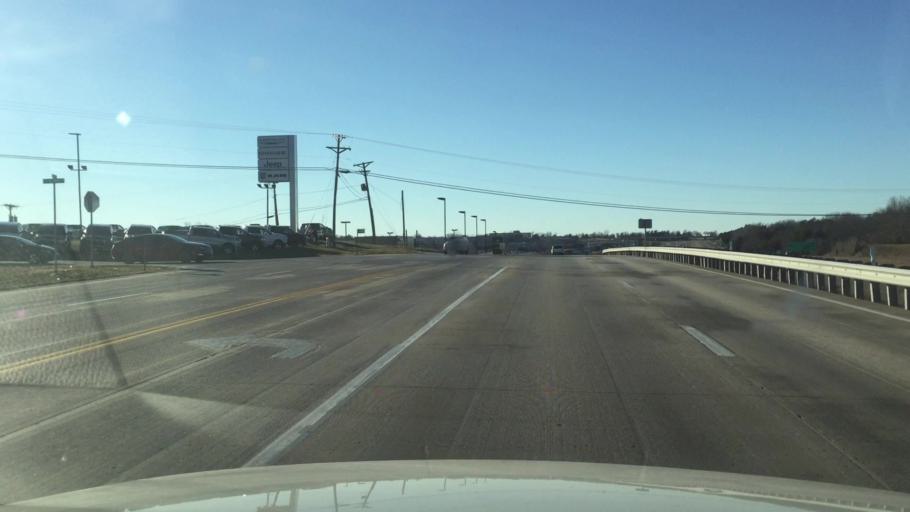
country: US
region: Missouri
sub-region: Cole County
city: Jefferson City
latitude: 38.5811
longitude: -92.2359
